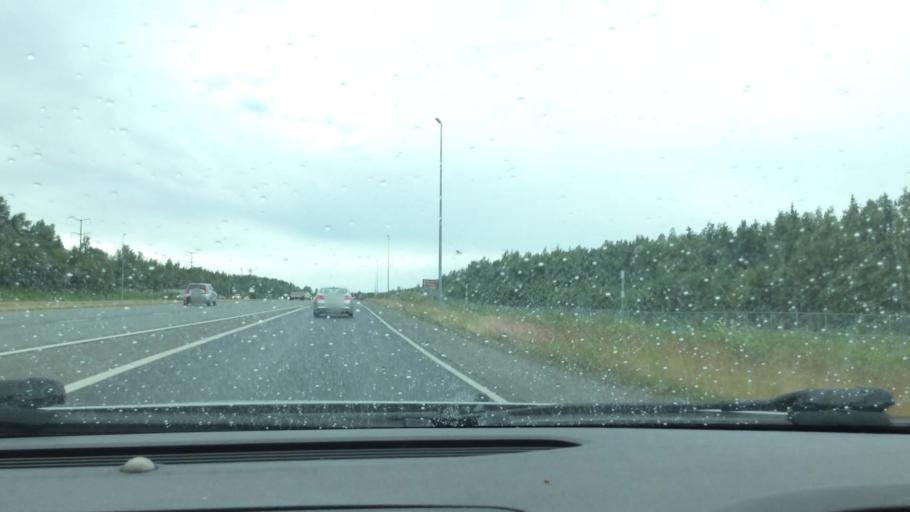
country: US
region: Alaska
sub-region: Anchorage Municipality
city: Elmendorf Air Force Base
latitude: 61.2522
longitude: -149.6634
